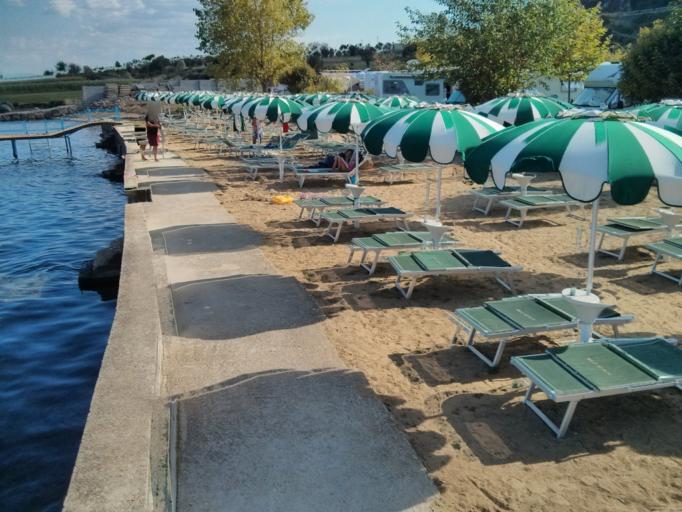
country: AL
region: Korce
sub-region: Rrethi i Pogradecit
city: Udenisht
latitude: 40.9669
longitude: 20.6430
